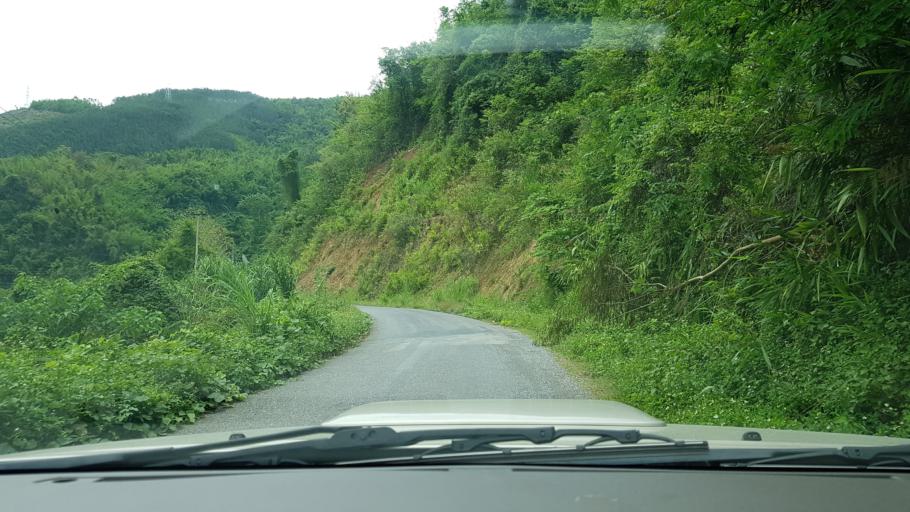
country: LA
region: Phongsali
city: Khoa
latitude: 21.0490
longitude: 102.4170
